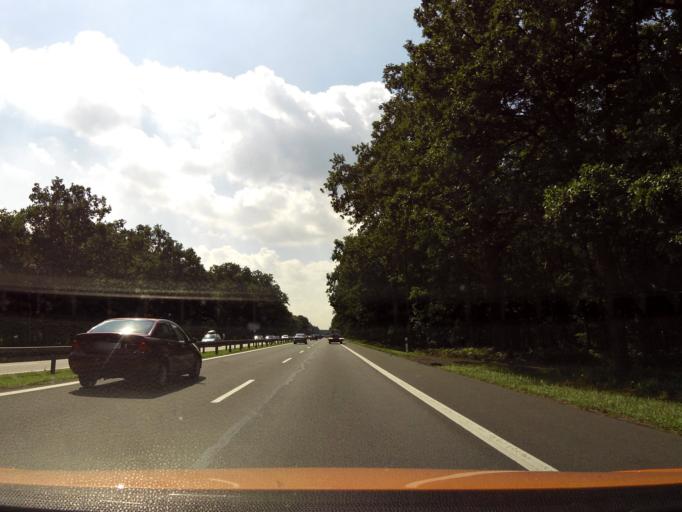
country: PL
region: West Pomeranian Voivodeship
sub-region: Powiat stargardzki
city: Kobylanka
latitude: 53.4402
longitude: 14.7791
